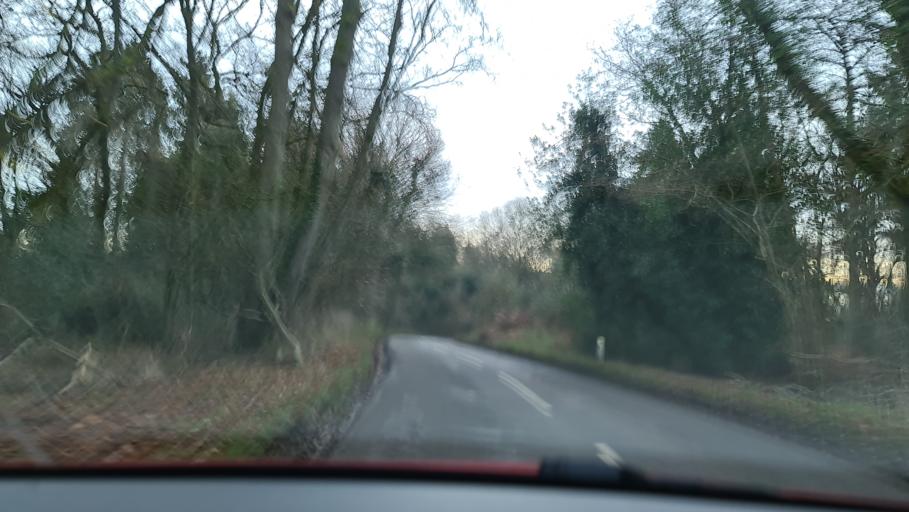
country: GB
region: England
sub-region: Buckinghamshire
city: Princes Risborough
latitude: 51.7071
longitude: -0.7838
